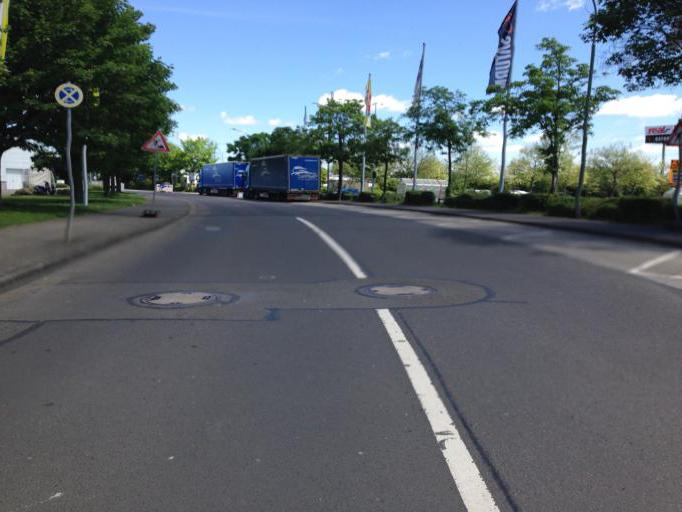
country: DE
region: Hesse
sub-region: Regierungsbezirk Giessen
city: Heuchelheim
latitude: 50.5808
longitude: 8.6469
